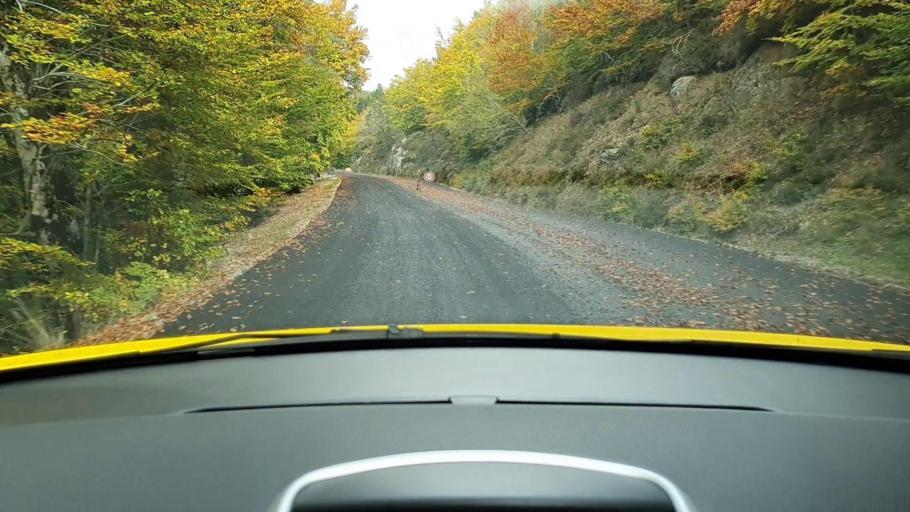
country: FR
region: Languedoc-Roussillon
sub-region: Departement du Gard
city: Valleraugue
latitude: 44.0799
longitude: 3.5361
